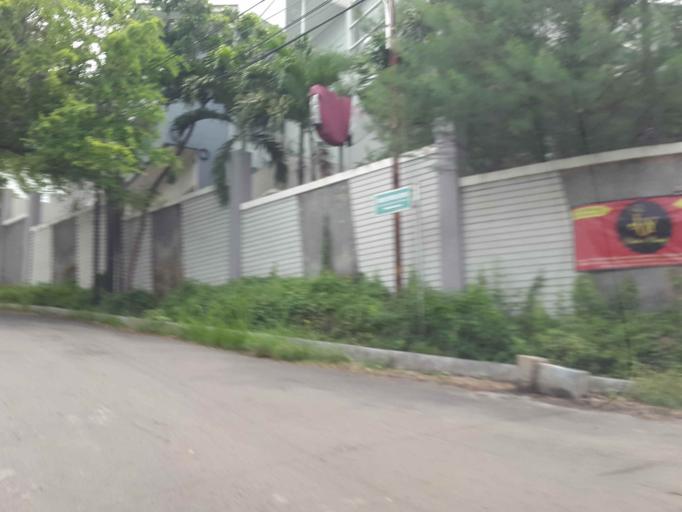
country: ID
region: Central Java
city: Semarang
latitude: -7.0110
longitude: 110.3996
